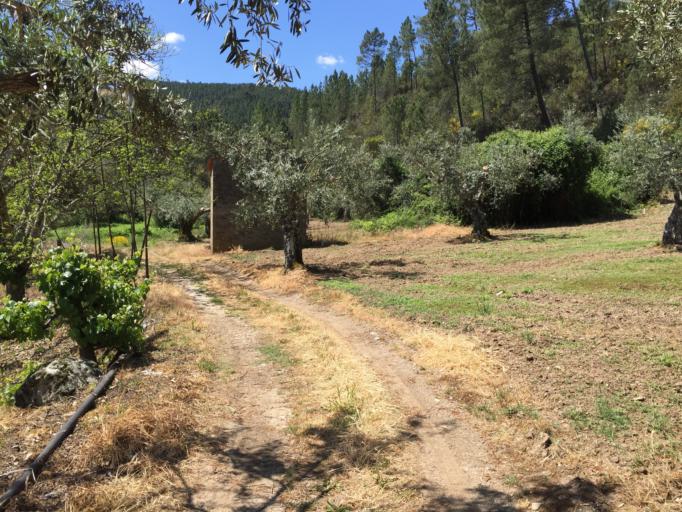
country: PT
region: Coimbra
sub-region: Pampilhosa da Serra
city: Pampilhosa da Serra
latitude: 40.0702
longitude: -7.7770
